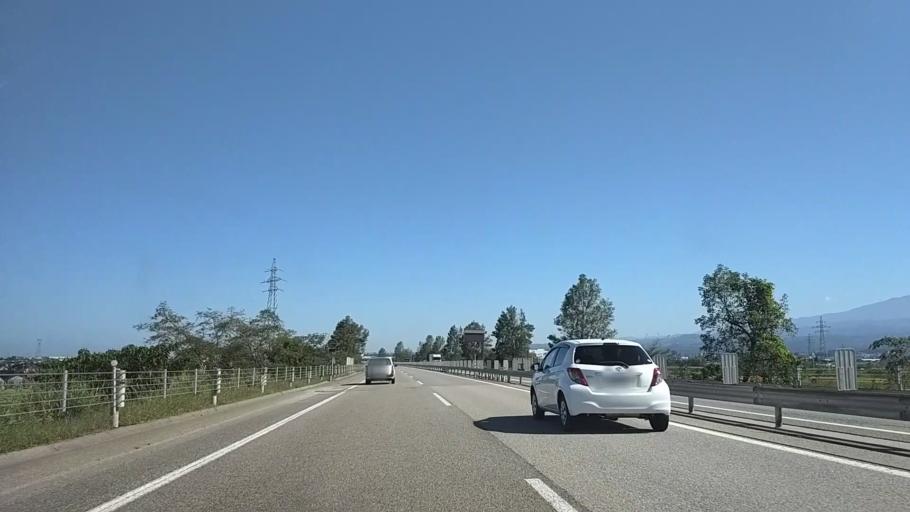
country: JP
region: Toyama
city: Kamiichi
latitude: 36.6879
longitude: 137.3272
